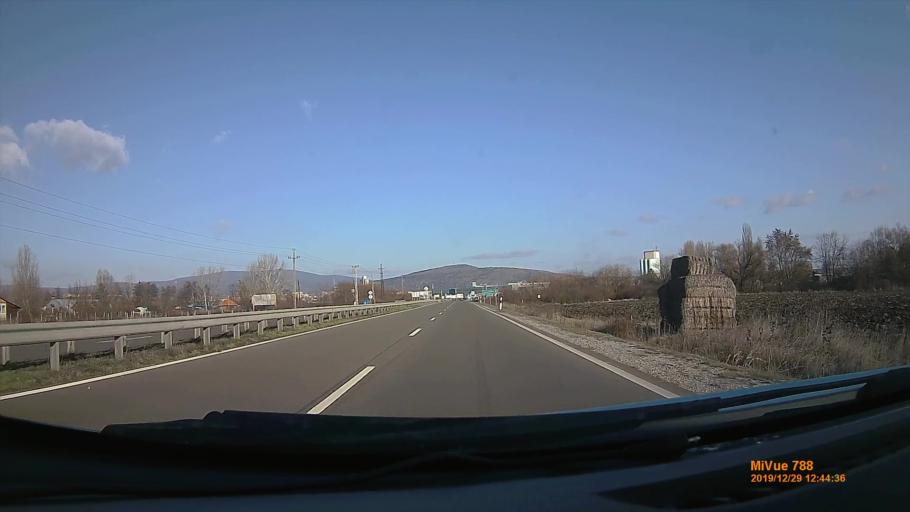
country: HU
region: Heves
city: Gyongyoshalasz
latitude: 47.7612
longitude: 19.9042
